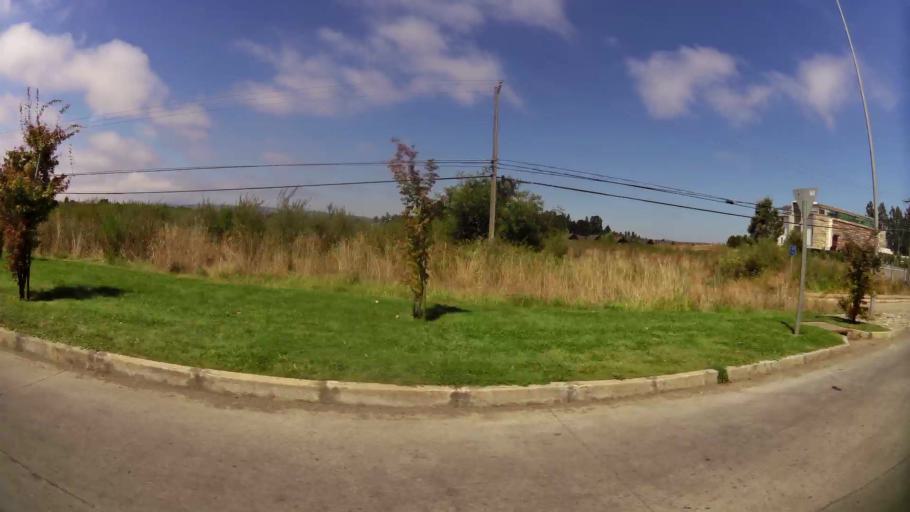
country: CL
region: Biobio
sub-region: Provincia de Concepcion
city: Concepcion
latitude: -36.7814
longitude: -73.0585
